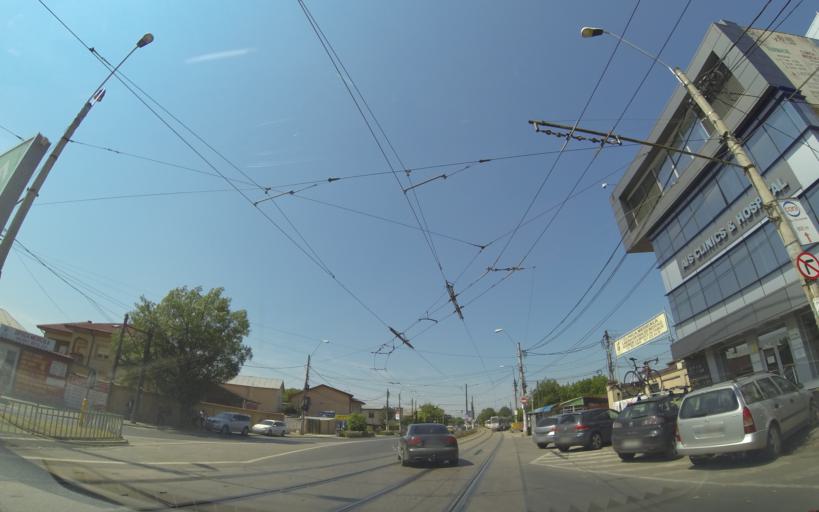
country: RO
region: Ilfov
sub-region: Comuna Magurele
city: Magurele
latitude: 44.3997
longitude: 26.0484
